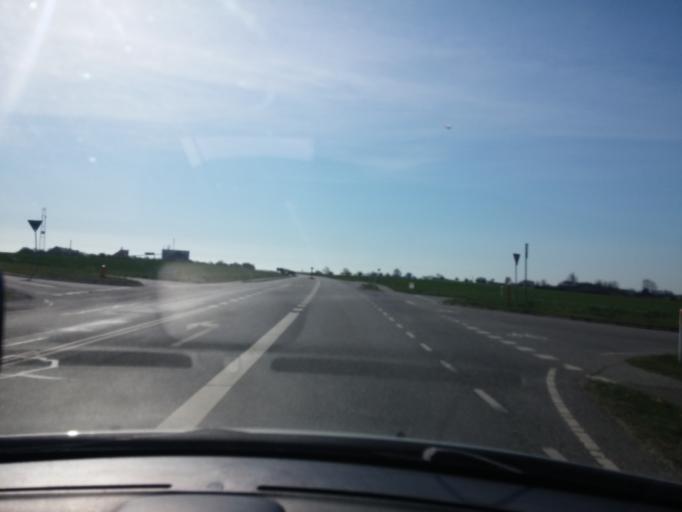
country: DK
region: Central Jutland
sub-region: Odder Kommune
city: Odder
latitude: 55.9412
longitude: 10.2111
